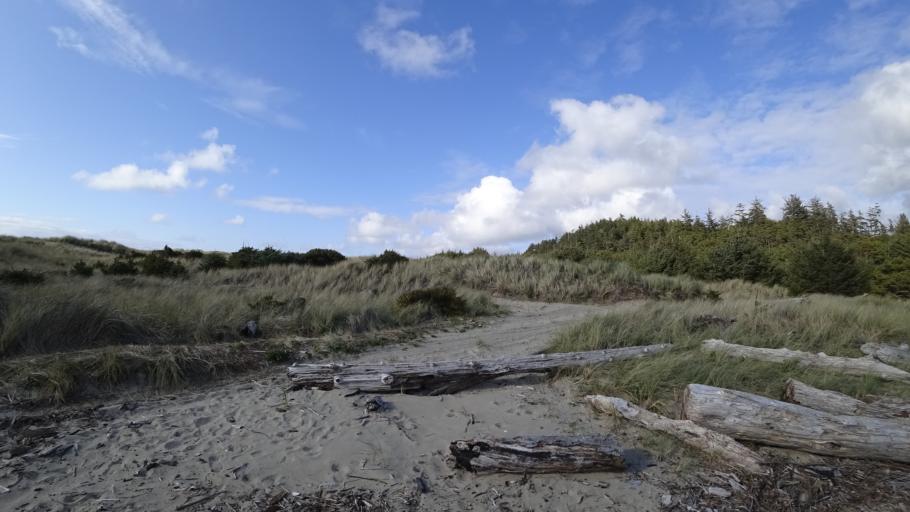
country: US
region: Oregon
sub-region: Douglas County
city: Reedsport
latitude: 43.7485
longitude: -124.1812
